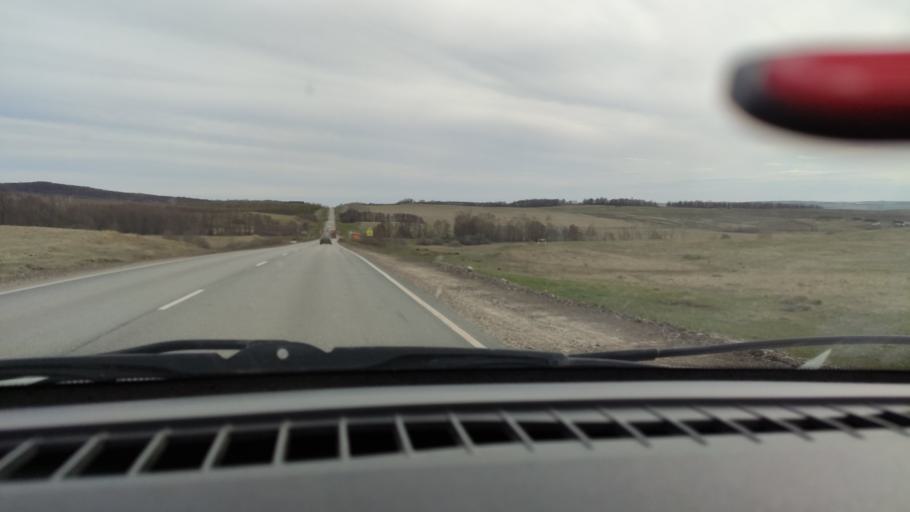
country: RU
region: Bashkortostan
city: Yermolayevo
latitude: 52.7326
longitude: 55.8582
